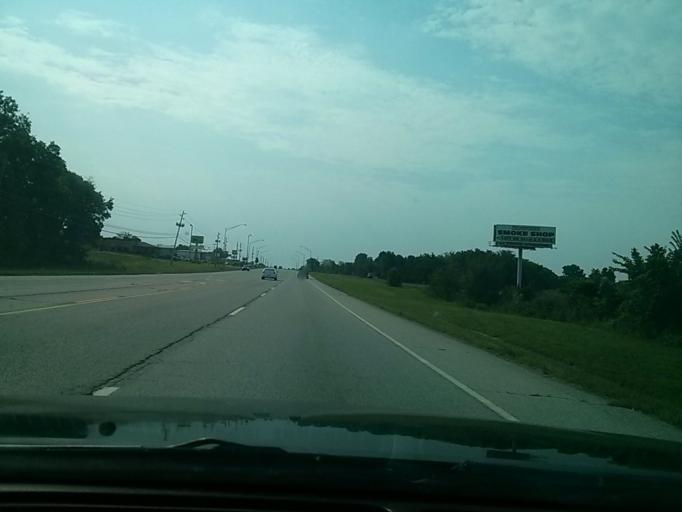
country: US
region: Oklahoma
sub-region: Wagoner County
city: Coweta
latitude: 35.9708
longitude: -95.6597
